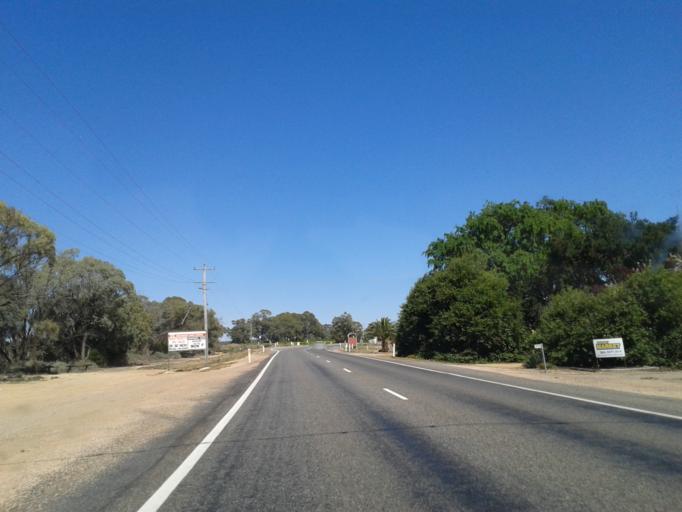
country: AU
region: New South Wales
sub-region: Wentworth
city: Dareton
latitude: -34.1112
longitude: 141.9767
